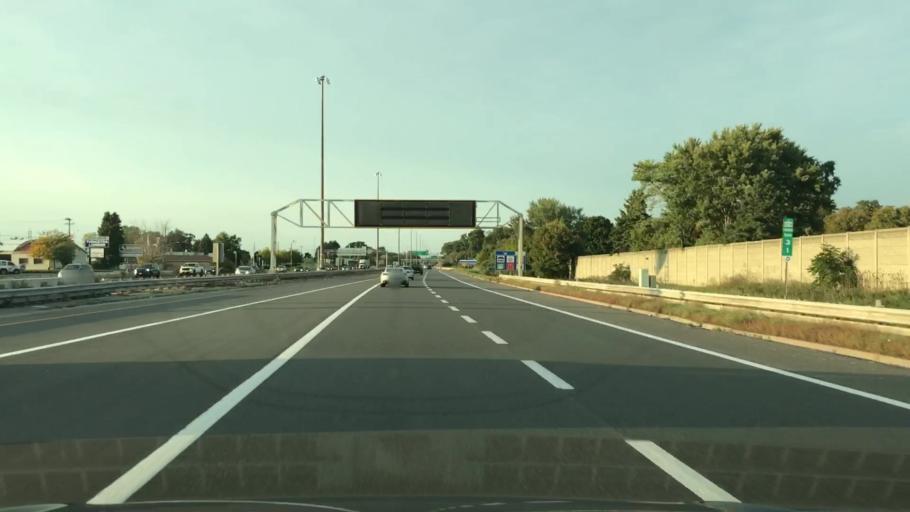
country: CA
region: Ontario
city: Niagara Falls
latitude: 43.1055
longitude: -79.1195
